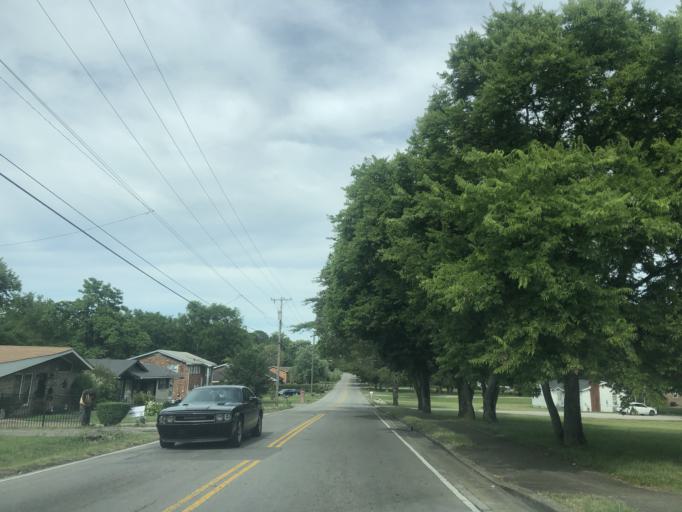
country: US
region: Tennessee
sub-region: Davidson County
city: Nashville
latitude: 36.2151
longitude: -86.8166
